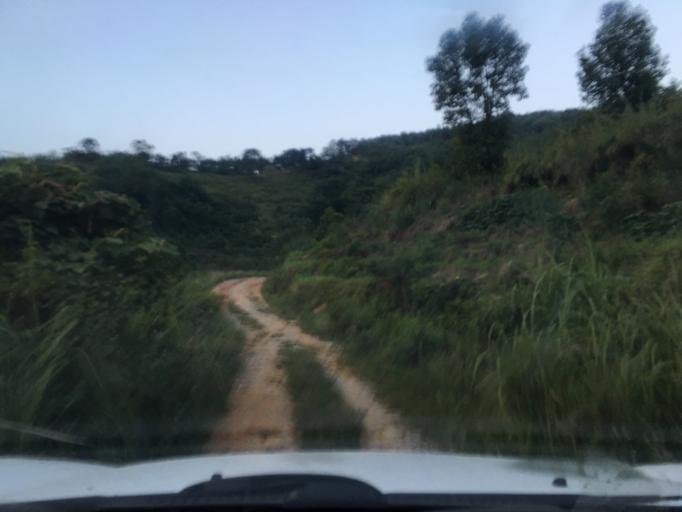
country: CN
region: Guangxi Zhuangzu Zizhiqu
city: Xinzhou
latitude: 25.3509
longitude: 105.7383
